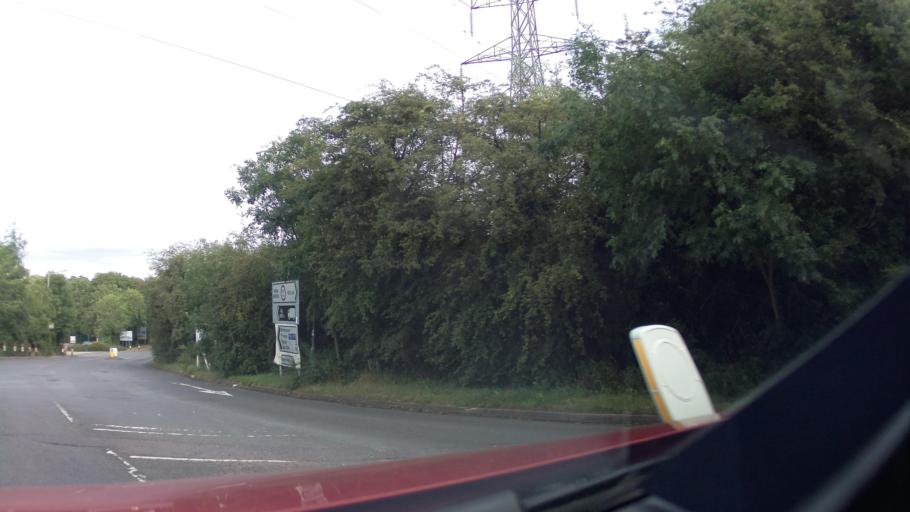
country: GB
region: England
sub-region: Warwickshire
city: Rugby
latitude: 52.3938
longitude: -1.2669
